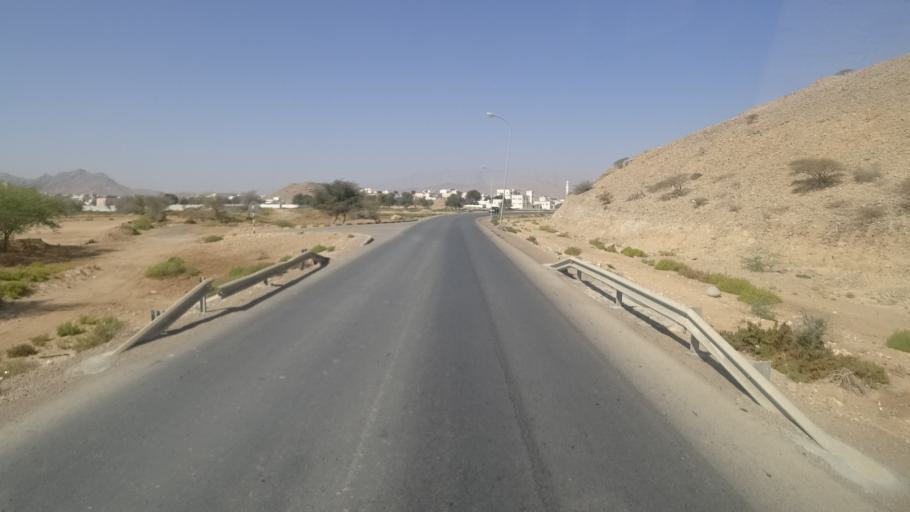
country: OM
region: Ash Sharqiyah
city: Sur
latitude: 22.5390
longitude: 59.4939
